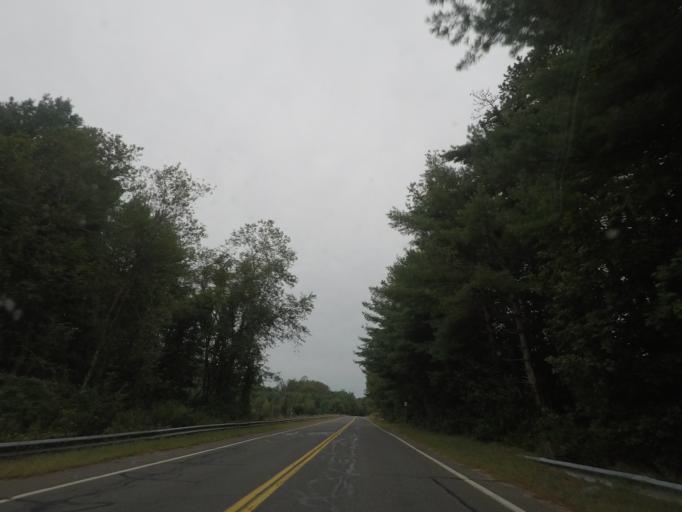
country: US
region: Massachusetts
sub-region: Hampden County
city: Palmer
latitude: 42.1856
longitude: -72.3077
